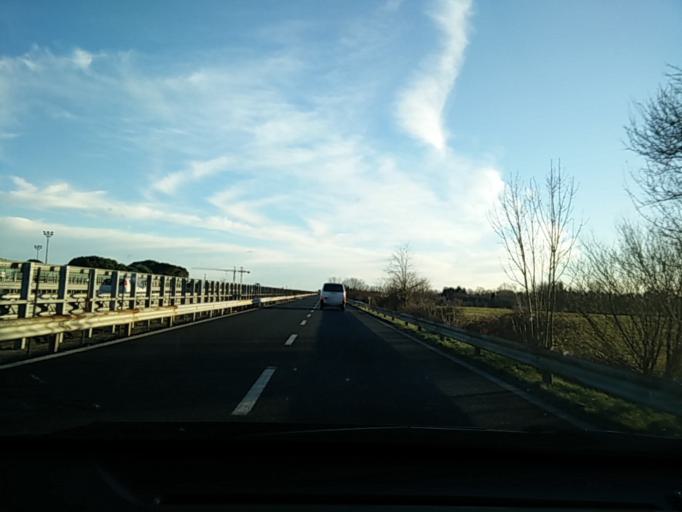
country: IT
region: Friuli Venezia Giulia
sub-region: Provincia di Udine
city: Colugna
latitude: 46.0948
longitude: 13.1967
